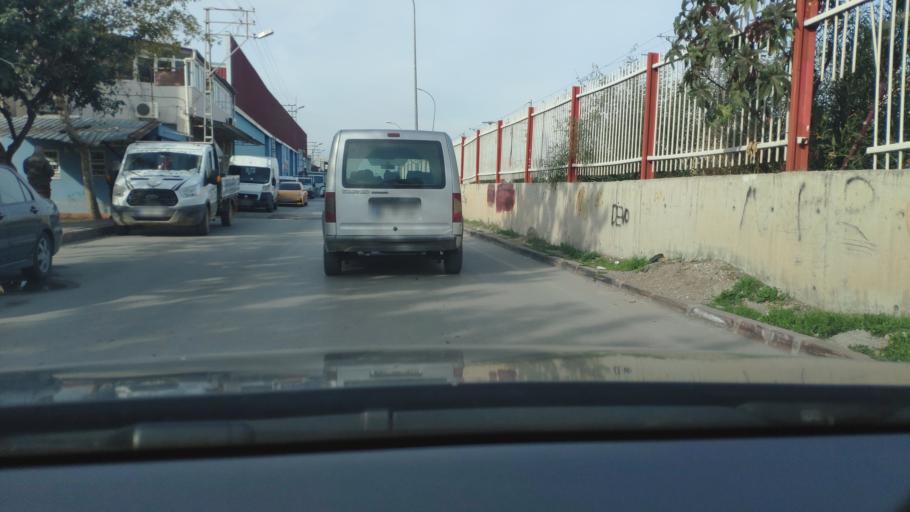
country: TR
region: Adana
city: Seyhan
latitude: 36.9973
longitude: 35.2742
